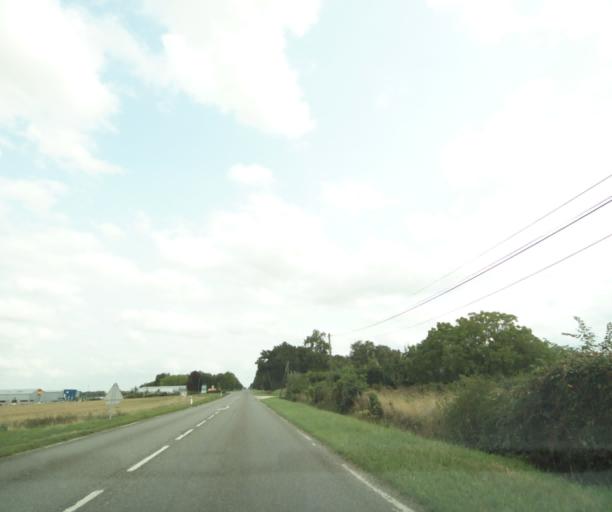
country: FR
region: Centre
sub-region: Departement de l'Indre
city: Buzancais
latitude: 46.8872
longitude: 1.4362
